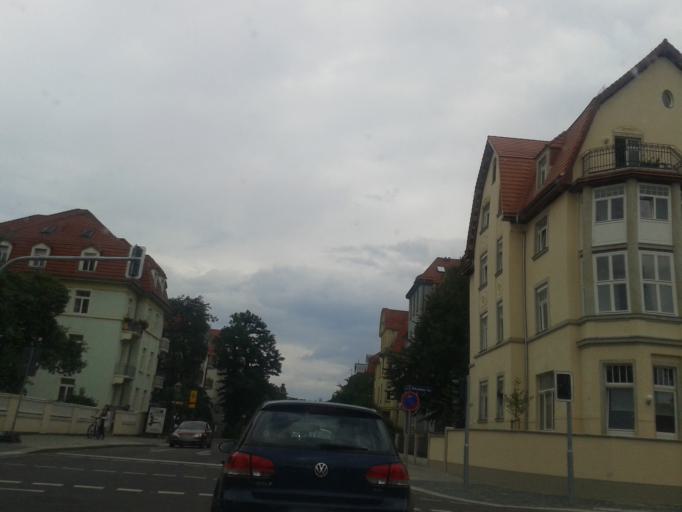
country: DE
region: Saxony
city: Albertstadt
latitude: 51.0429
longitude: 13.7955
